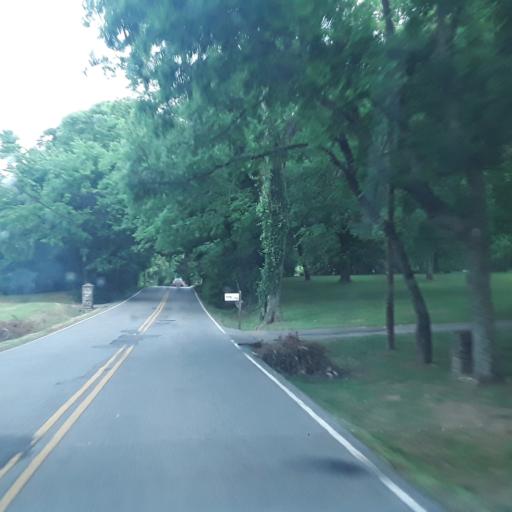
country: US
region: Tennessee
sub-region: Williamson County
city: Brentwood
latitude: 36.0502
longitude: -86.7687
